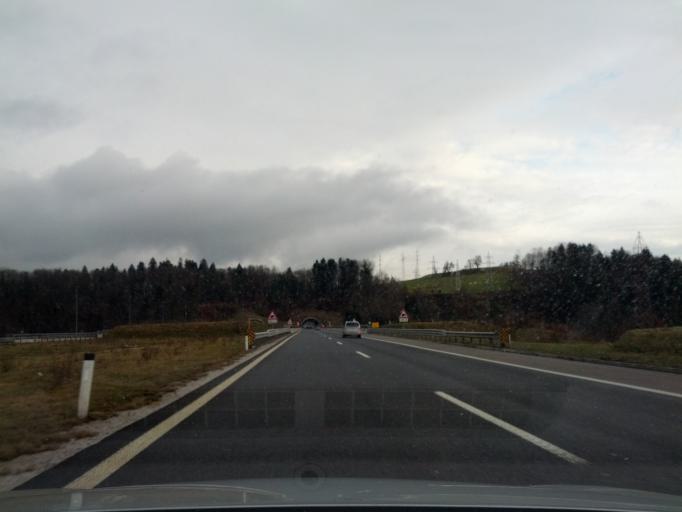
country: SI
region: Trzic
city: Bistrica pri Trzicu
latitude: 46.3212
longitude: 14.2379
